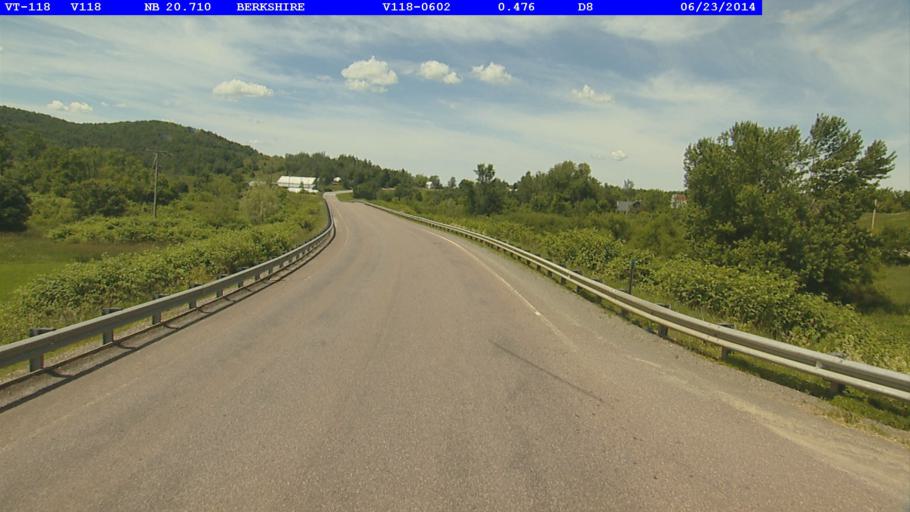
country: US
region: Vermont
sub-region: Franklin County
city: Richford
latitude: 44.9306
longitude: -72.6919
